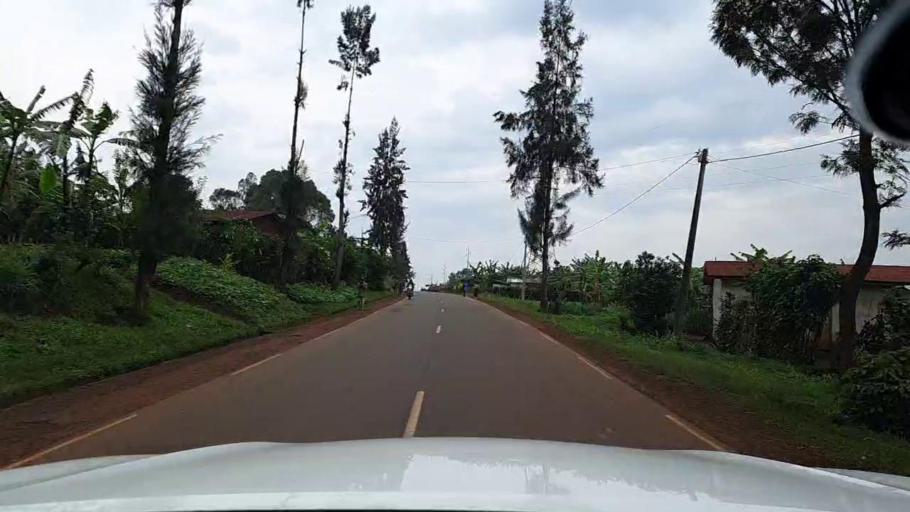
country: RW
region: Western Province
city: Cyangugu
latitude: -2.6180
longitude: 28.9450
